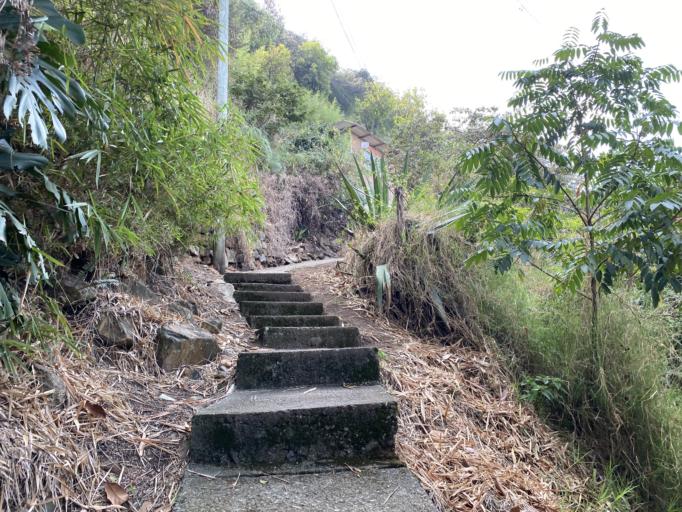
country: CO
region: Antioquia
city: Medellin
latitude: 6.2816
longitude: -75.5435
